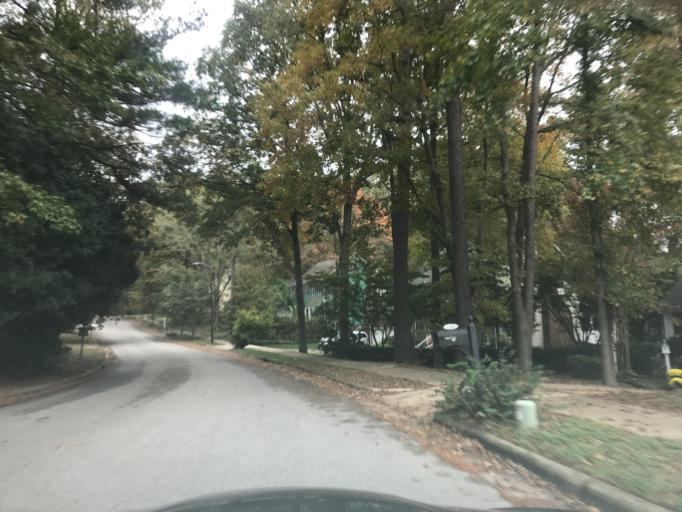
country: US
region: North Carolina
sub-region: Wake County
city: West Raleigh
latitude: 35.8908
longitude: -78.6338
